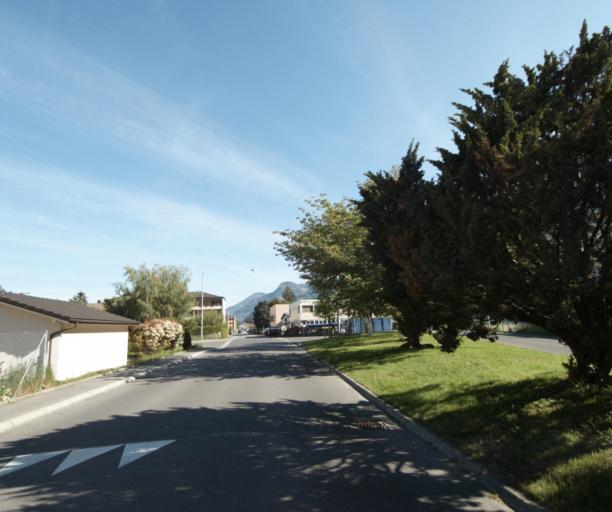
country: CH
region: Vaud
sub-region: Aigle District
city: Villeneuve
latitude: 46.3925
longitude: 6.9299
